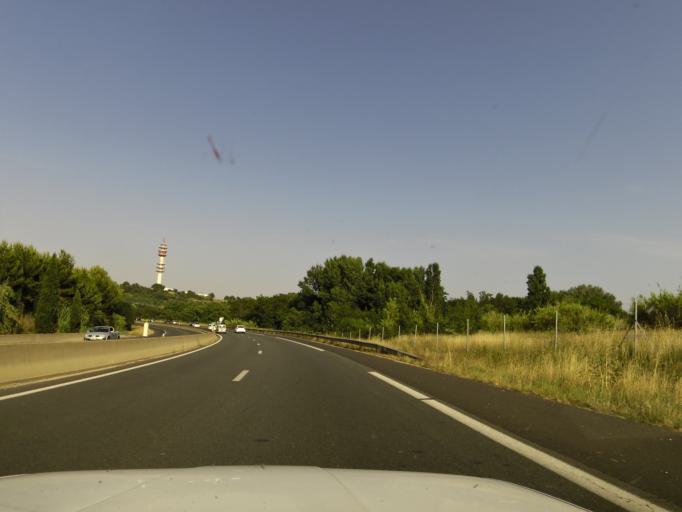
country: FR
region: Languedoc-Roussillon
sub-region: Departement de l'Herault
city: Juvignac
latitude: 43.6055
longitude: 3.8127
